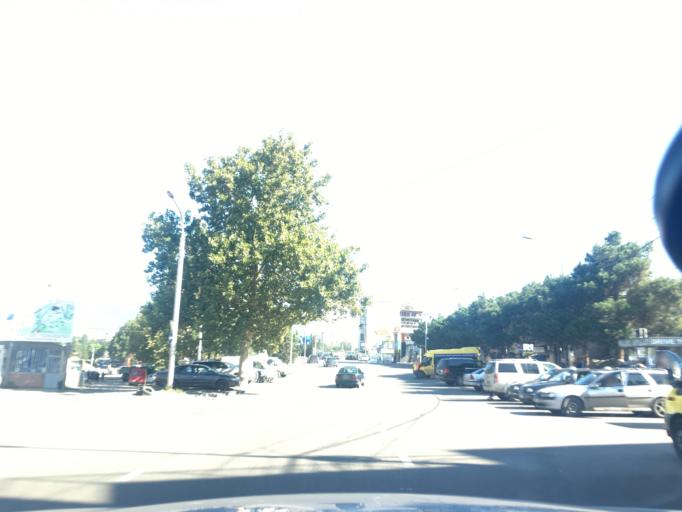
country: GE
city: Zahesi
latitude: 41.7834
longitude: 44.7990
